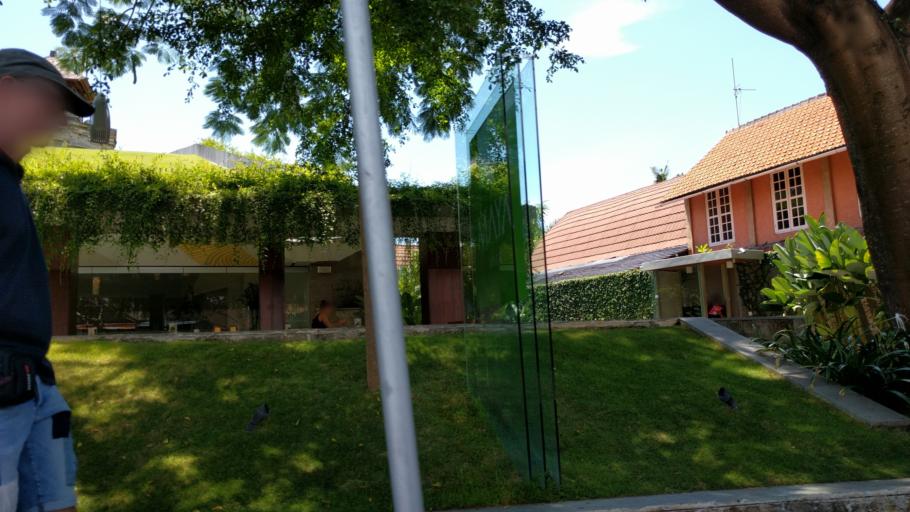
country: ID
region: Bali
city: Banjar Medura
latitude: -8.6977
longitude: 115.2632
